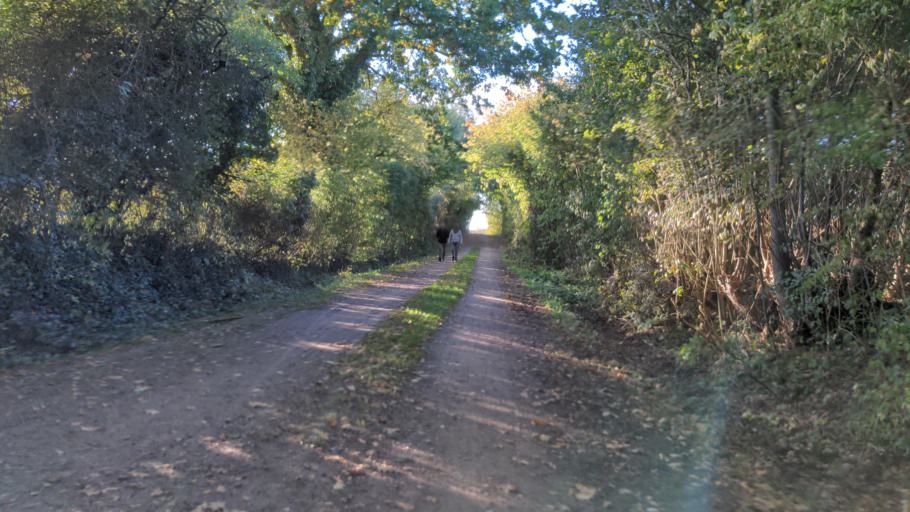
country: DE
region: Schleswig-Holstein
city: Neustadt in Holstein
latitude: 54.0967
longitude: 10.8495
